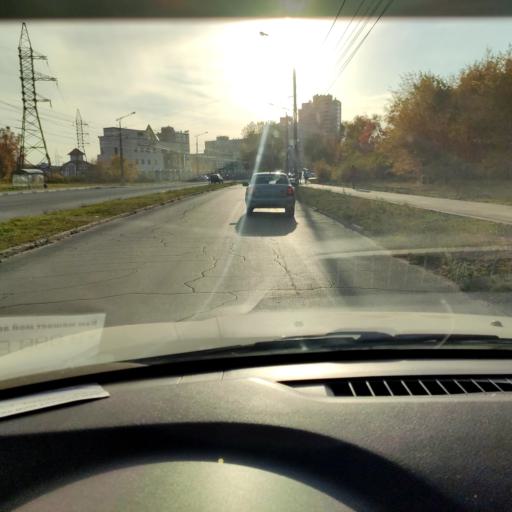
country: RU
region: Samara
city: Tol'yatti
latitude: 53.5022
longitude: 49.4263
